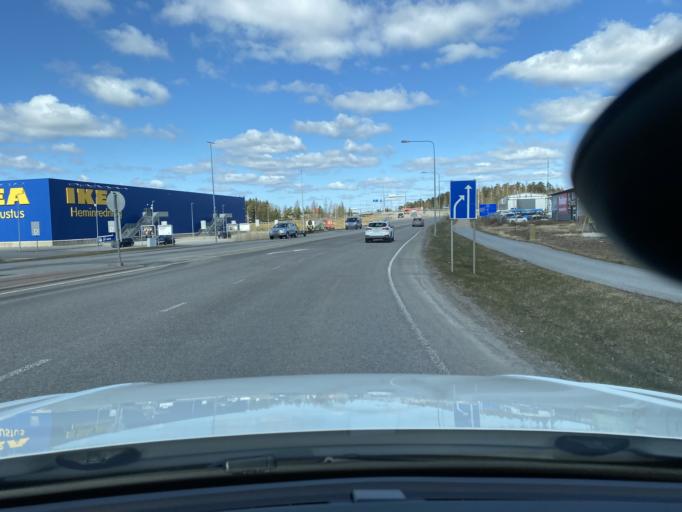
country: FI
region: Varsinais-Suomi
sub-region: Turku
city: Rusko
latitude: 60.4936
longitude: 22.2311
